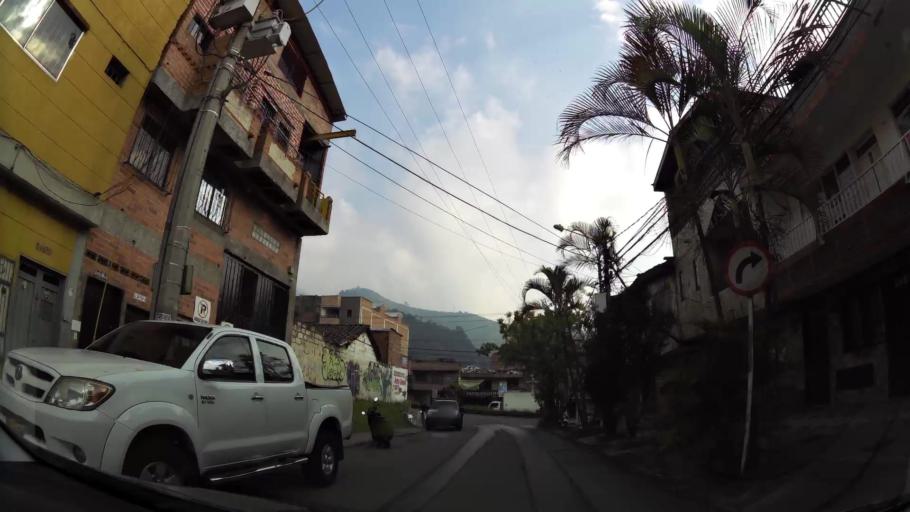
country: CO
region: Antioquia
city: Sabaneta
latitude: 6.1686
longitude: -75.6238
